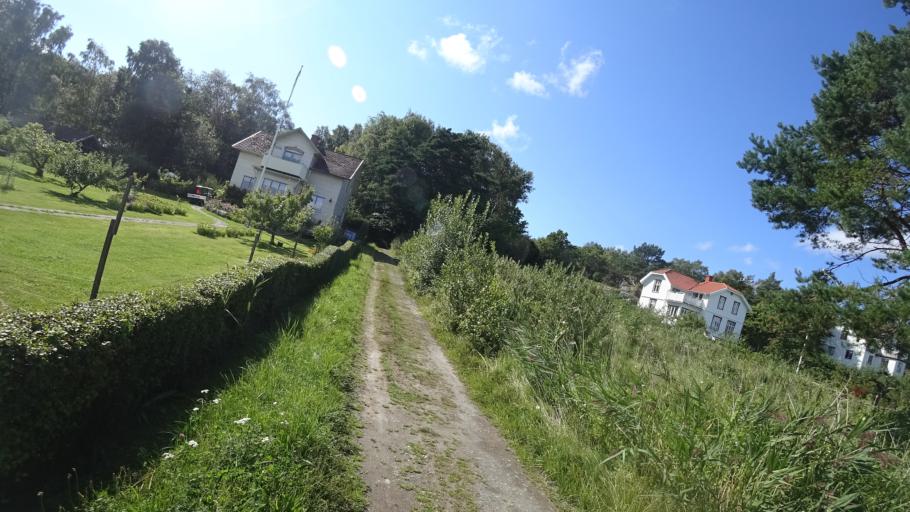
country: SE
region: Vaestra Goetaland
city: Donso
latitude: 57.6058
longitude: 11.7898
